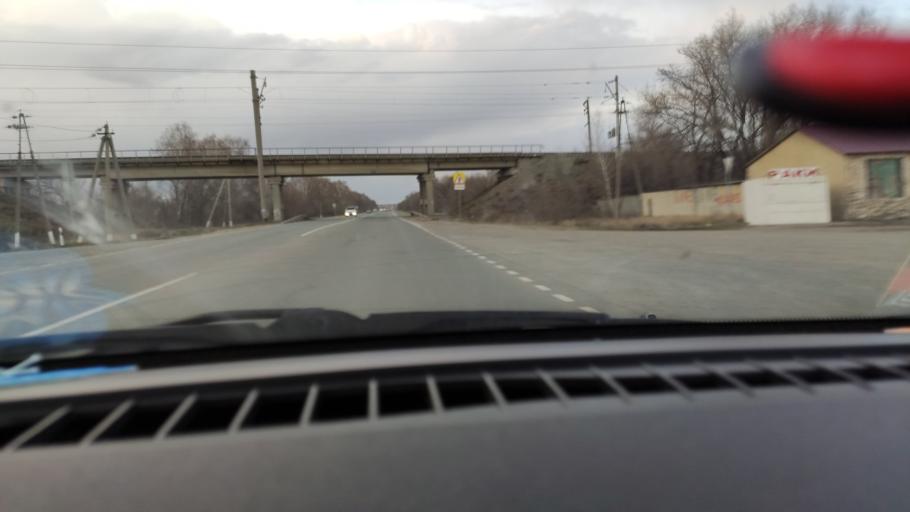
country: RU
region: Saratov
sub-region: Saratovskiy Rayon
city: Saratov
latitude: 51.7004
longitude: 46.0109
